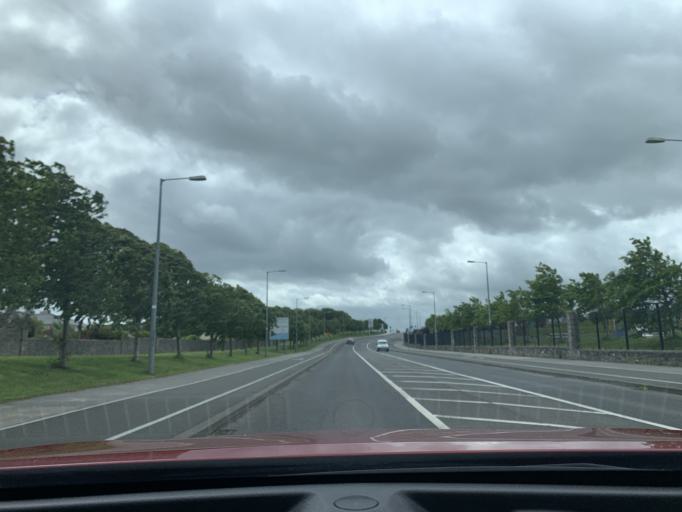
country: IE
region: Connaught
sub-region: Sligo
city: Sligo
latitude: 54.2690
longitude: -8.5027
